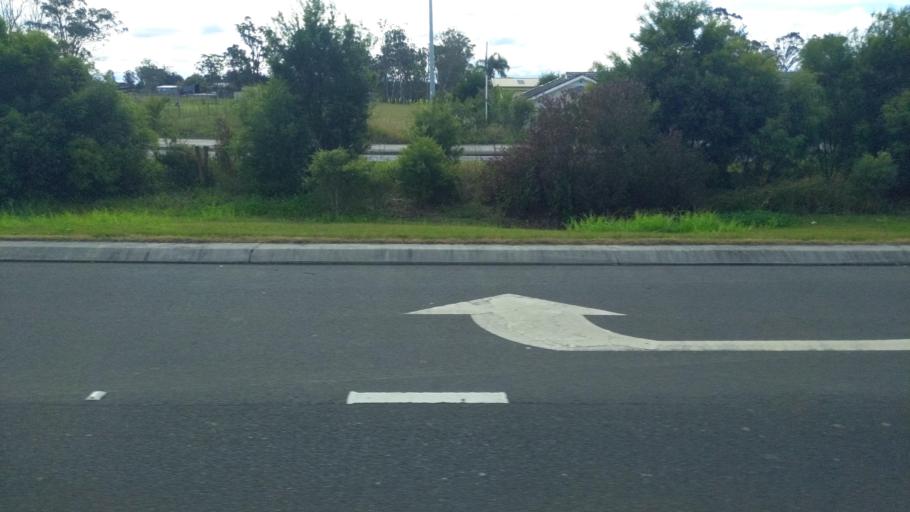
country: AU
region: New South Wales
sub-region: Blacktown
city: Hassall Grove
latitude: -33.7062
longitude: 150.8444
